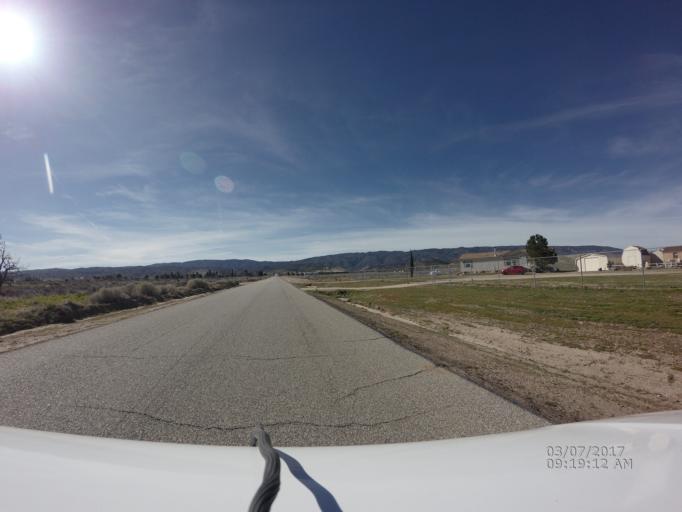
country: US
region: California
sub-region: Los Angeles County
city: Green Valley
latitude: 34.7825
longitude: -118.5899
